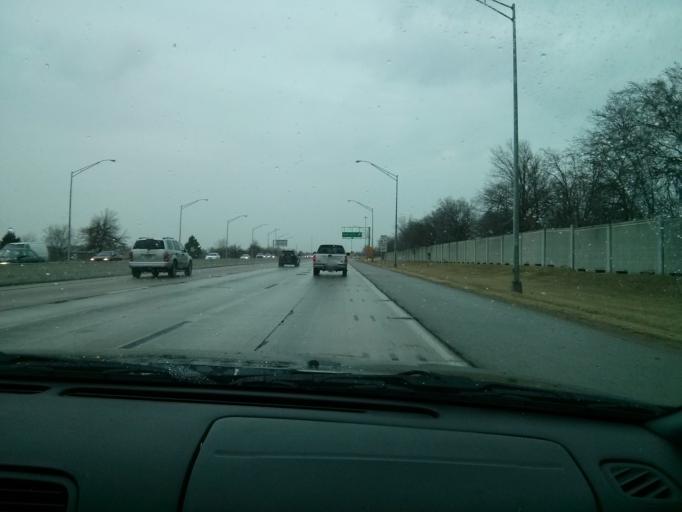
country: US
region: Oklahoma
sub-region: Tulsa County
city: Broken Arrow
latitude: 36.1130
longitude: -95.8596
